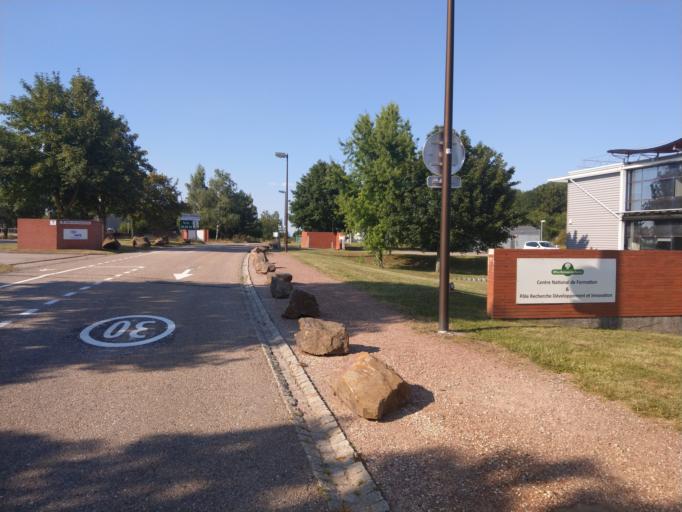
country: FR
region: Lorraine
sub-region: Departement de Meurthe-et-Moselle
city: Villers-les-Nancy
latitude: 48.6557
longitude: 6.1381
